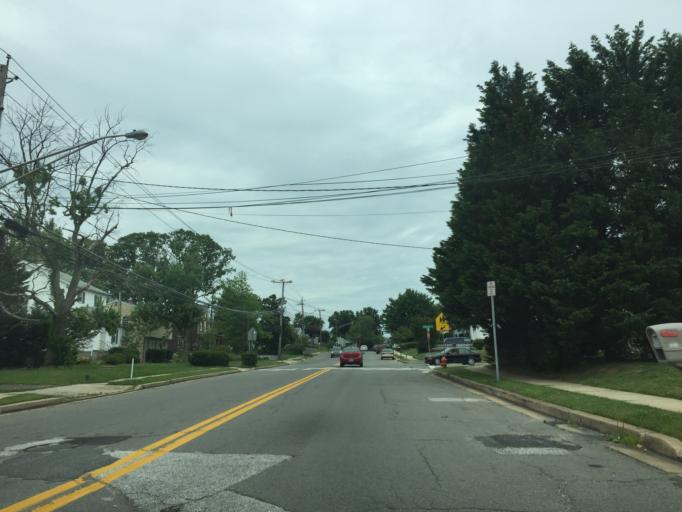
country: US
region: Maryland
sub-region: Baltimore County
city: Carney
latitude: 39.3995
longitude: -76.5346
